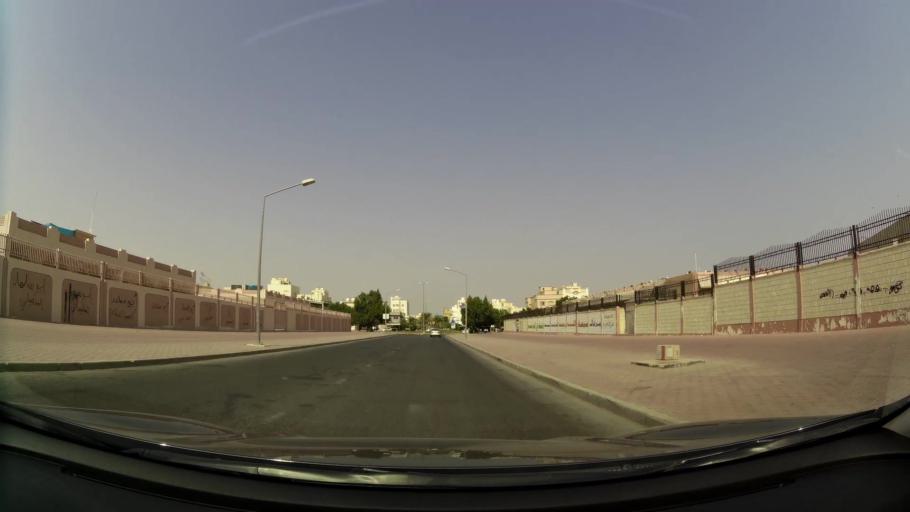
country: KW
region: Muhafazat al Jahra'
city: Al Jahra'
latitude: 29.3298
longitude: 47.6508
